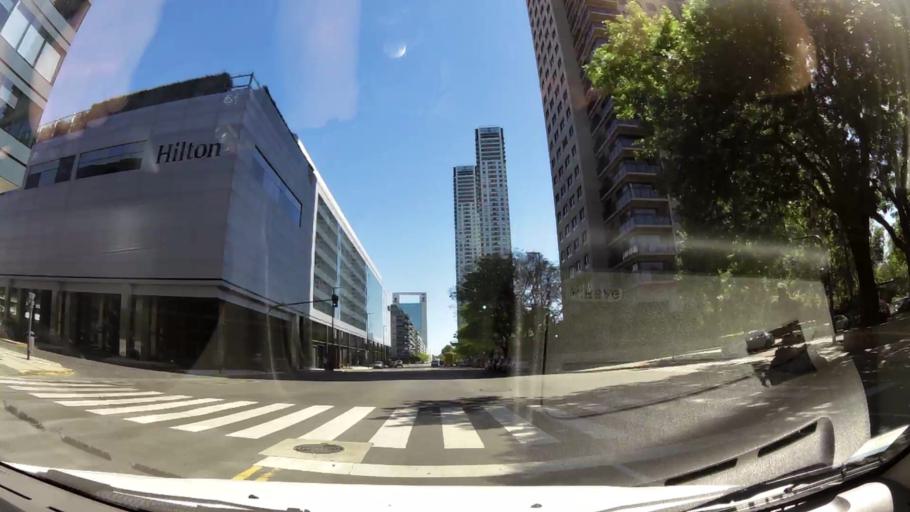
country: AR
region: Buenos Aires F.D.
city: Buenos Aires
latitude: -34.6067
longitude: -58.3632
